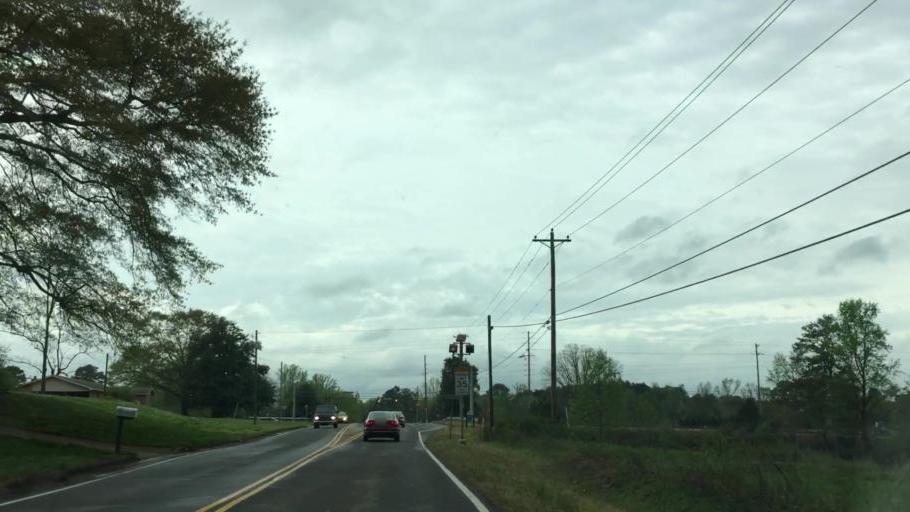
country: US
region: Georgia
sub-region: Cherokee County
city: Canton
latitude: 34.2109
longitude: -84.3957
